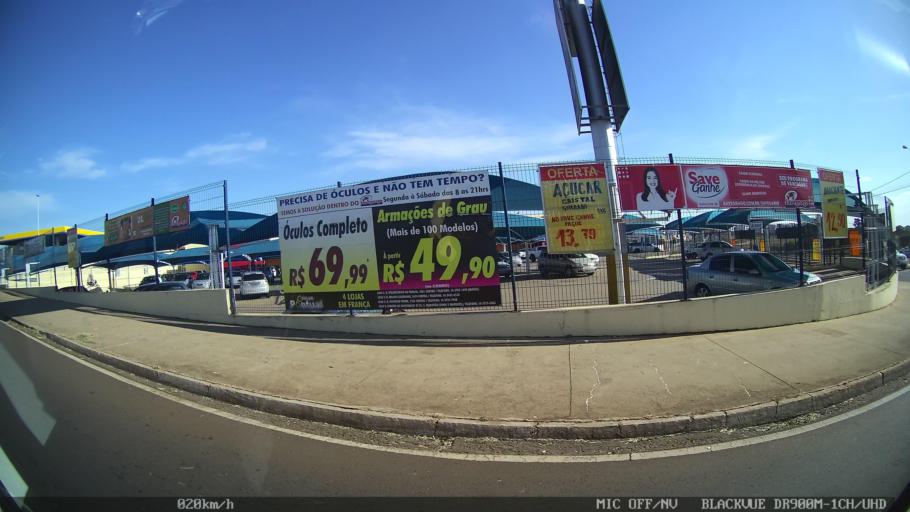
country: BR
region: Sao Paulo
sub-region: Franca
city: Franca
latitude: -20.5261
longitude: -47.4324
